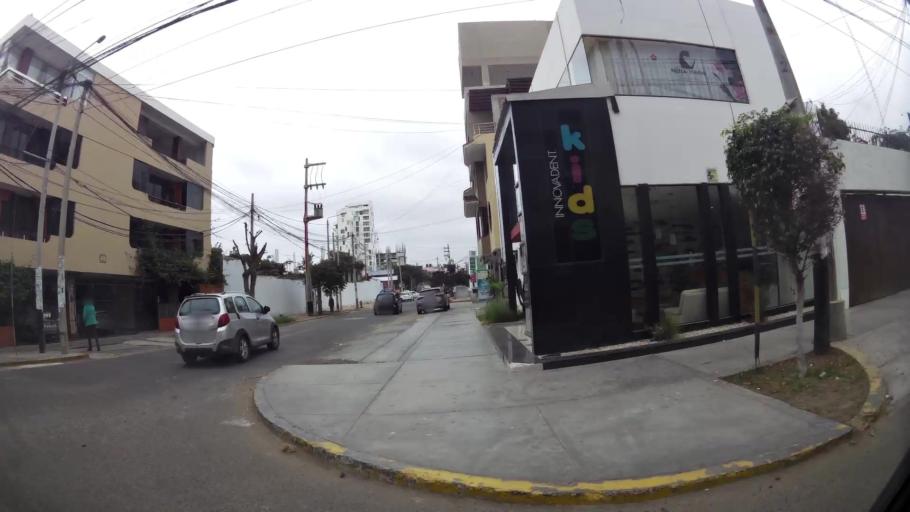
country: PE
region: La Libertad
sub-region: Provincia de Trujillo
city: Trujillo
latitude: -8.1169
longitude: -79.0311
